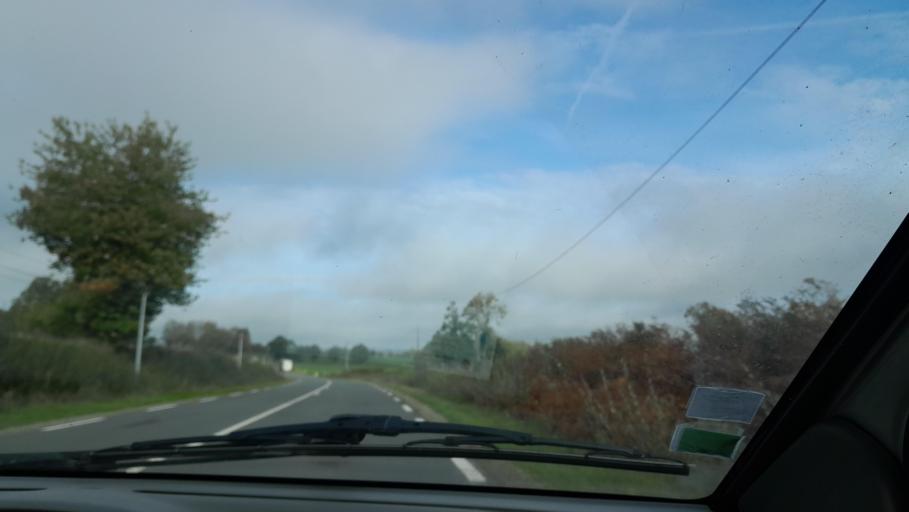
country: FR
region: Brittany
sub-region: Departement d'Ille-et-Vilaine
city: Luitre
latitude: 48.2928
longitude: -1.1577
